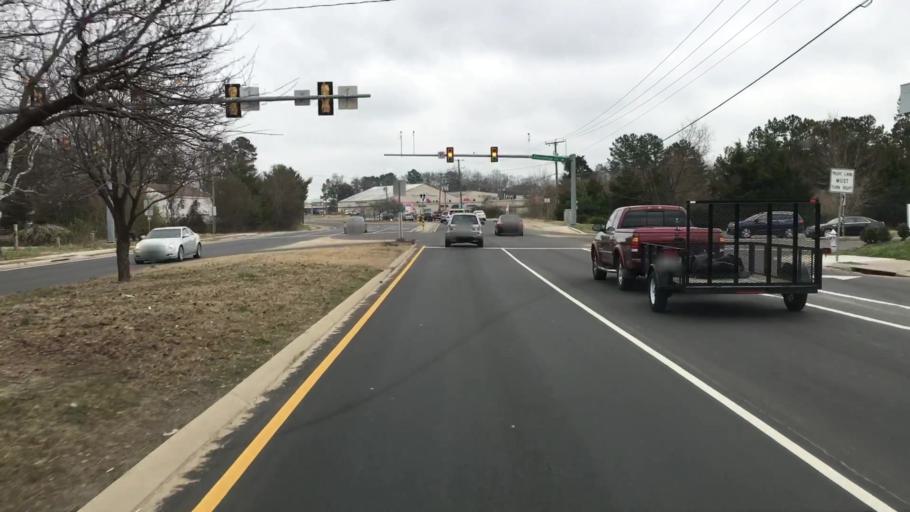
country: US
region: Virginia
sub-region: Chesterfield County
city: Bon Air
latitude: 37.5093
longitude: -77.5854
